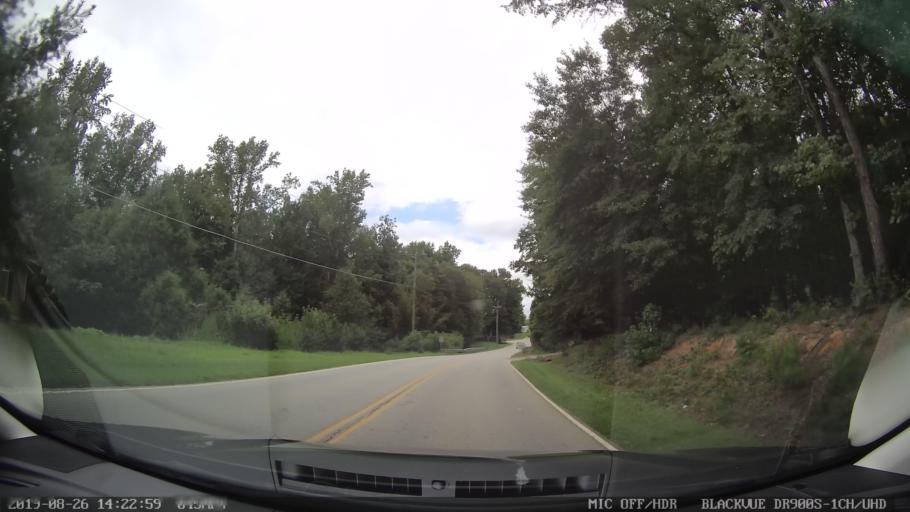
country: US
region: South Carolina
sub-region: Greenville County
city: Five Forks
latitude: 34.7895
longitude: -82.2681
